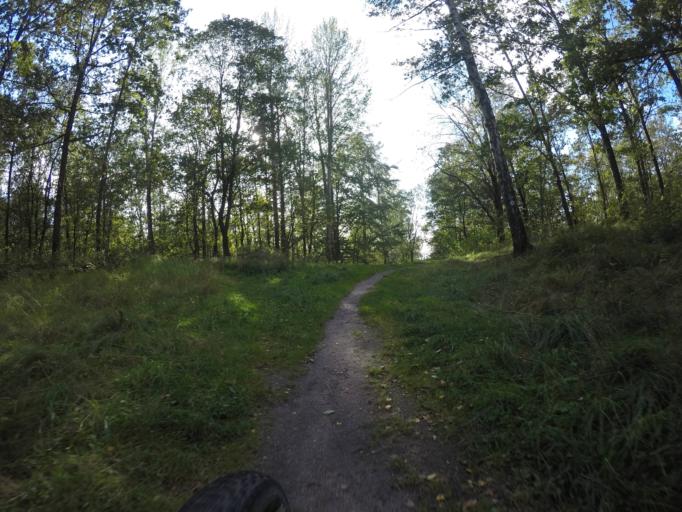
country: SE
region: Vaestmanland
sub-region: Kopings Kommun
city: Koping
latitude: 59.5122
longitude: 16.0080
